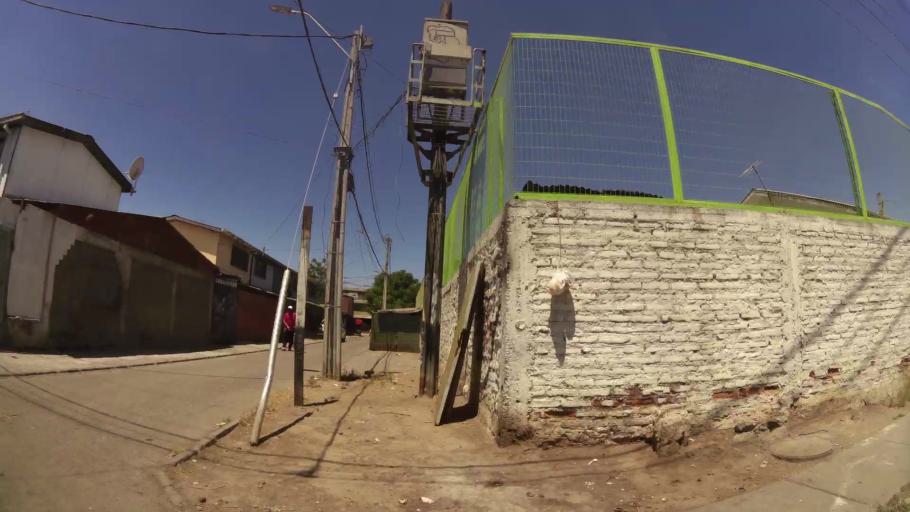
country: CL
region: Santiago Metropolitan
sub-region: Provincia de Maipo
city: San Bernardo
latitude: -33.5973
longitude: -70.6784
